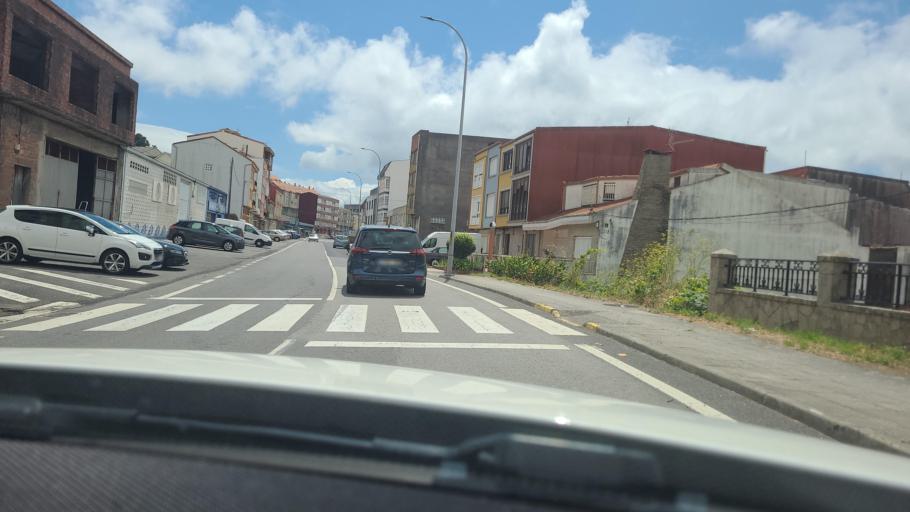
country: ES
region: Galicia
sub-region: Provincia da Coruna
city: Cee
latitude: 42.9536
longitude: -9.1868
